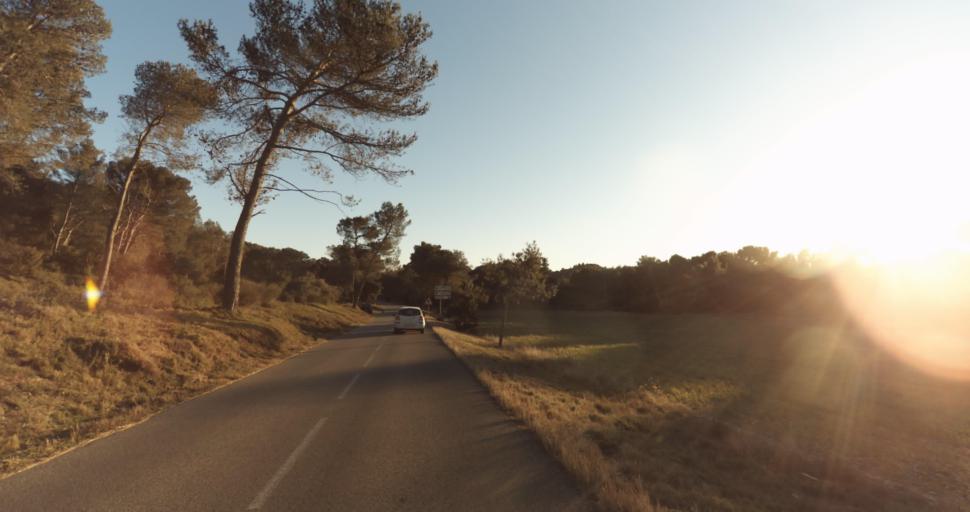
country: FR
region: Provence-Alpes-Cote d'Azur
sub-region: Departement des Bouches-du-Rhone
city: Boulbon
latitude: 43.8681
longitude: 4.7290
